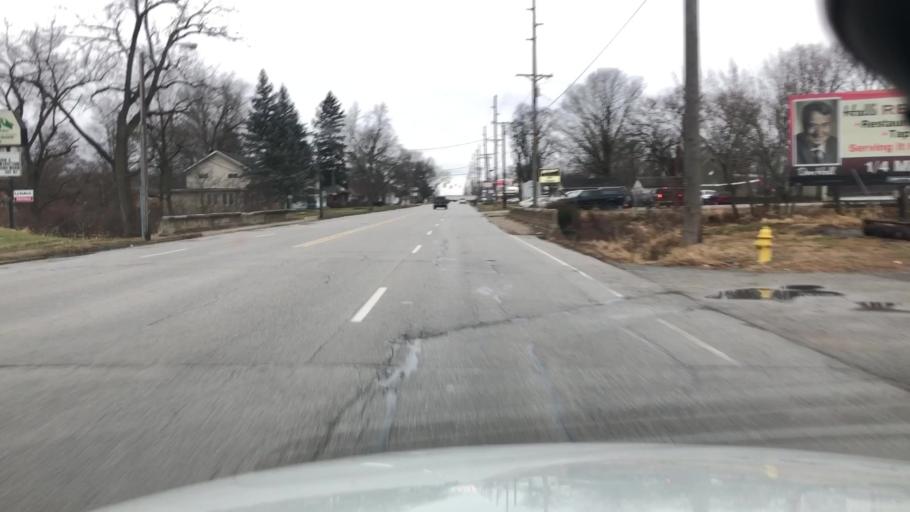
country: US
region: Indiana
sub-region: Allen County
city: New Haven
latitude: 41.0702
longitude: -85.0264
